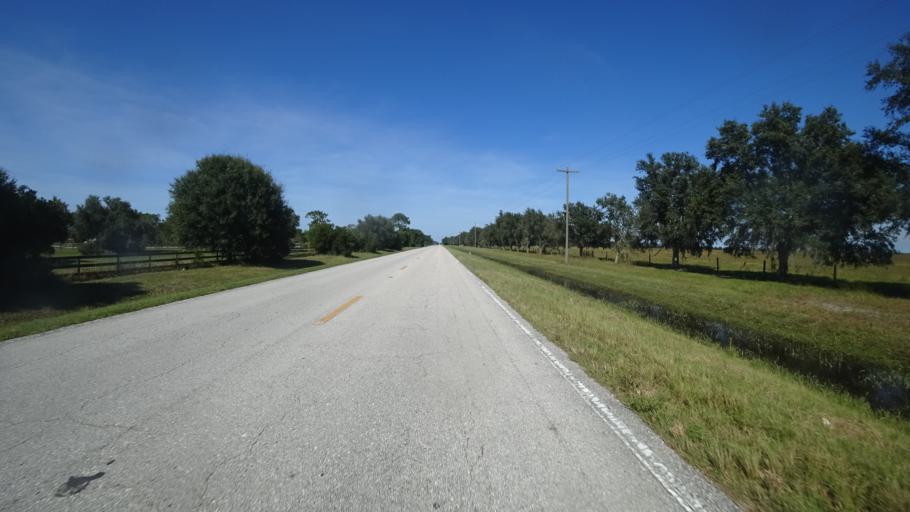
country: US
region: Florida
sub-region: Sarasota County
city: The Meadows
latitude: 27.4167
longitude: -82.3037
